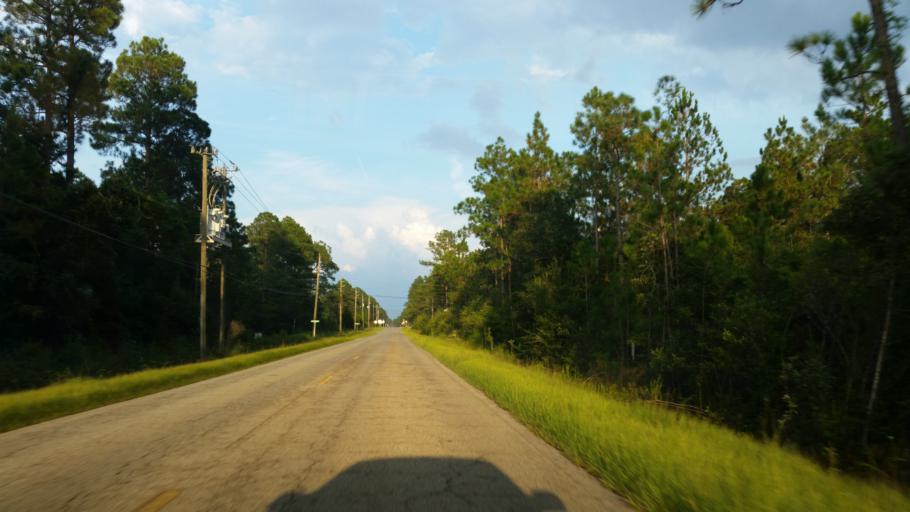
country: US
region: Florida
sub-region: Santa Rosa County
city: Bagdad
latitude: 30.5442
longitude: -87.0917
